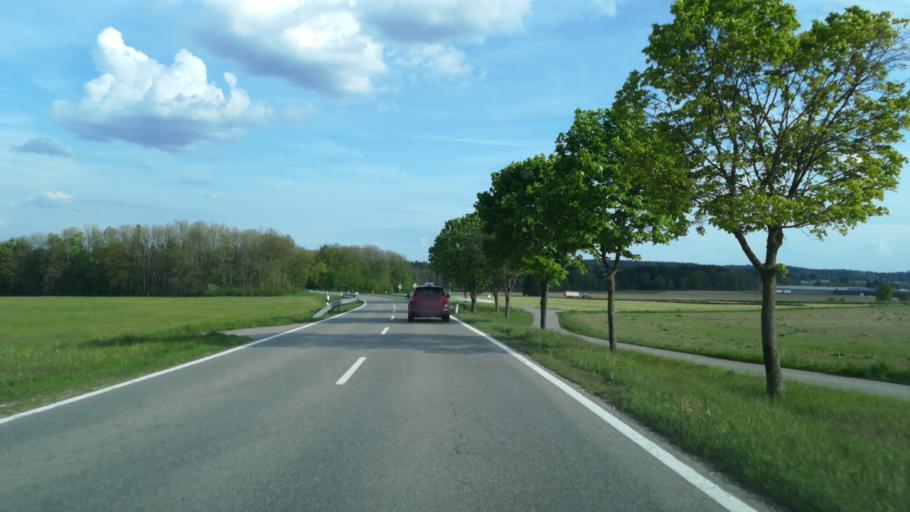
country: DE
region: Baden-Wuerttemberg
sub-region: Freiburg Region
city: Muhlingen
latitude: 47.9278
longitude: 9.0492
